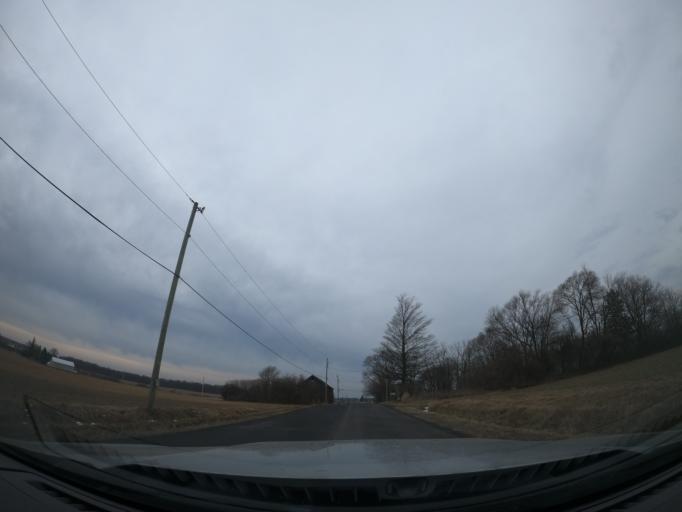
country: US
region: New York
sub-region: Cayuga County
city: Melrose Park
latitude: 42.8393
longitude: -76.5564
